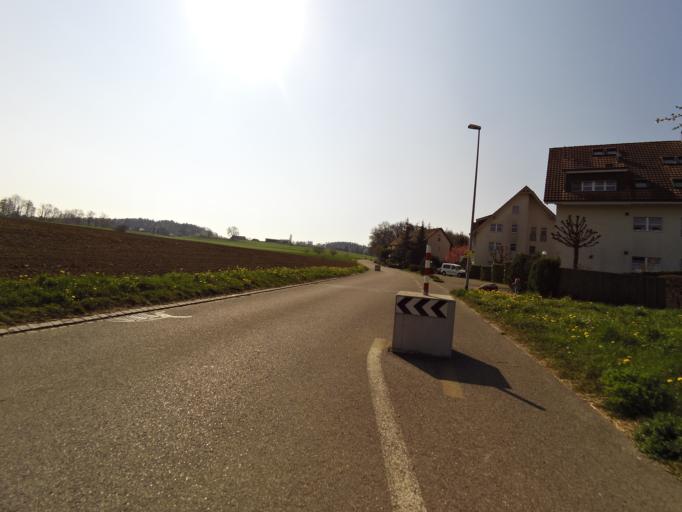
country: CH
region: Thurgau
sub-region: Frauenfeld District
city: Gachnang
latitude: 47.5490
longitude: 8.8621
